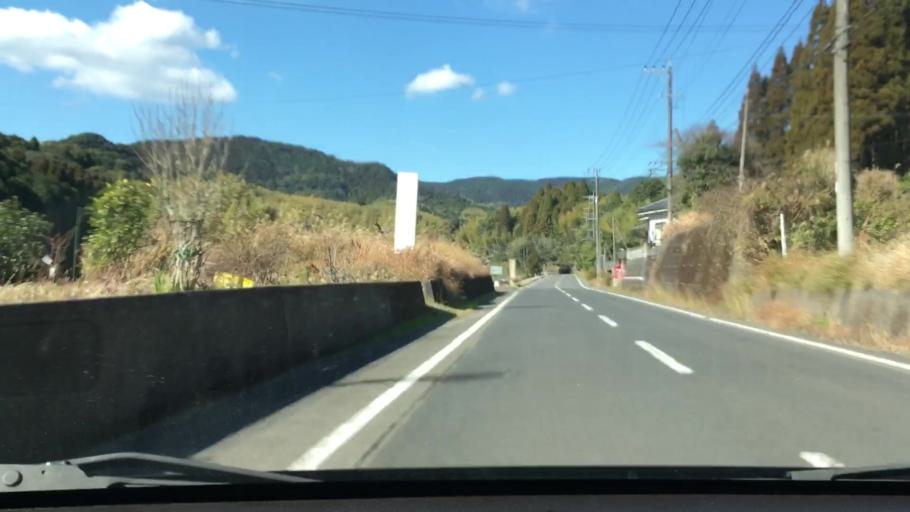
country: JP
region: Kagoshima
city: Ijuin
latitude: 31.7049
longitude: 130.4464
